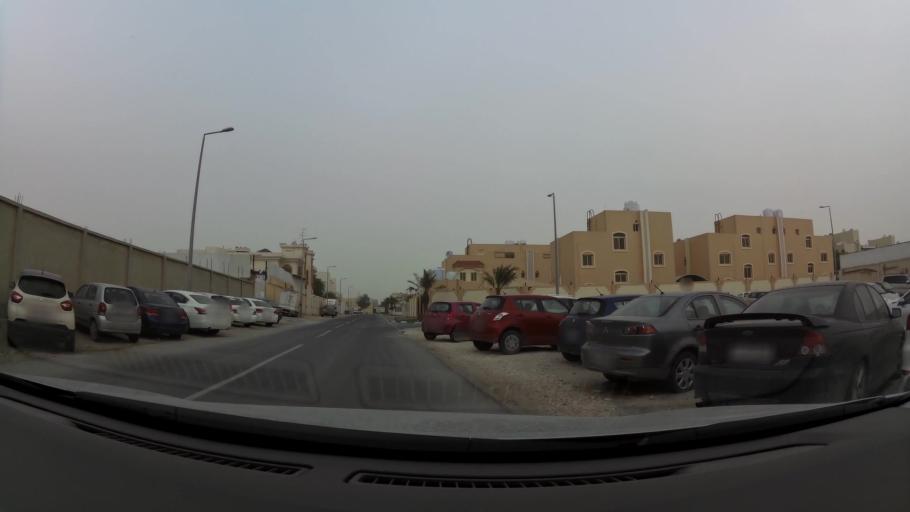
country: QA
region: Baladiyat ad Dawhah
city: Doha
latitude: 25.2535
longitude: 51.4822
